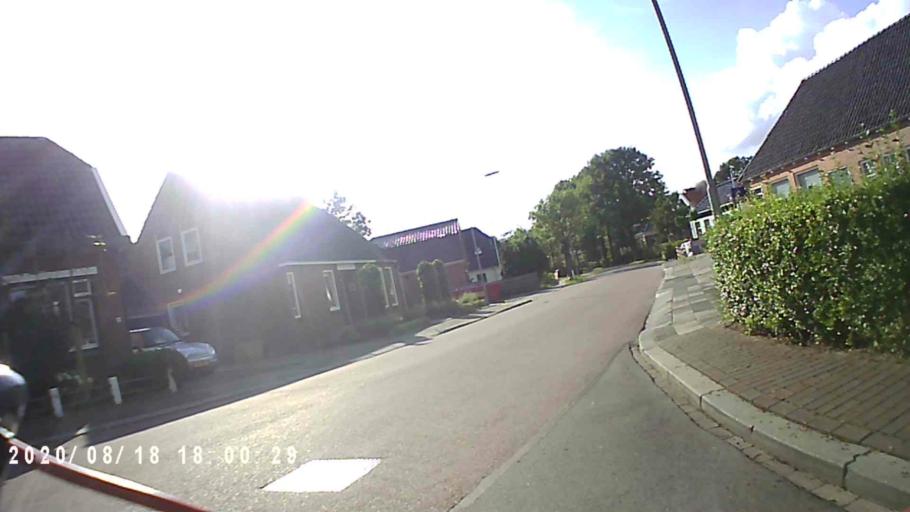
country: NL
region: Groningen
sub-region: Gemeente Zuidhorn
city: Noordhorn
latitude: 53.2626
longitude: 6.3943
